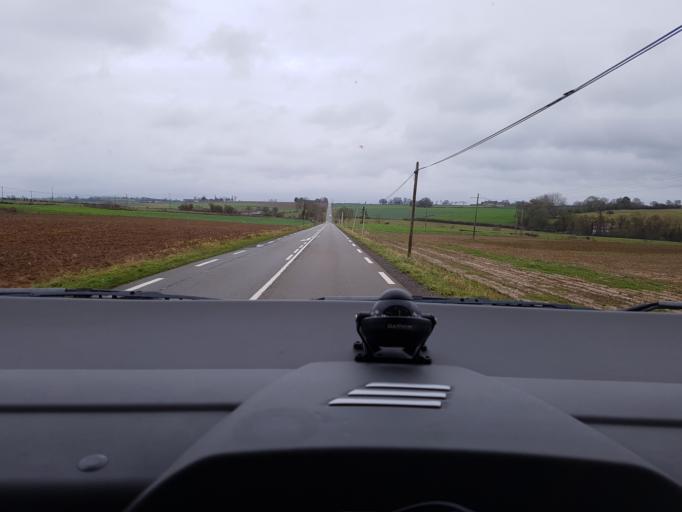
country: FR
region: Haute-Normandie
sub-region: Departement de la Seine-Maritime
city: Gournay-en-Bray
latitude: 49.4937
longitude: 1.7643
